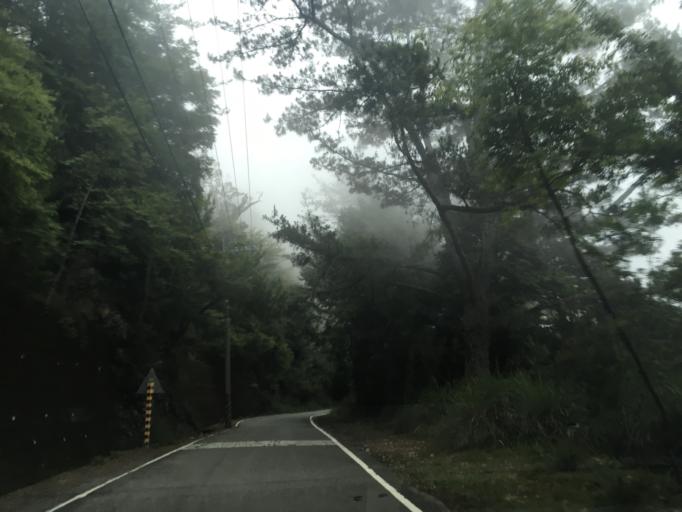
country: TW
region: Taiwan
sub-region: Nantou
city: Puli
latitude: 24.2555
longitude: 121.0093
